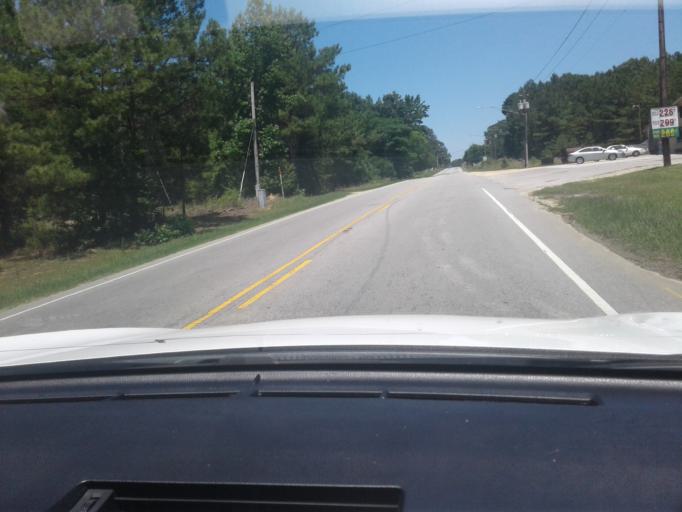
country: US
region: North Carolina
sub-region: Harnett County
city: Erwin
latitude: 35.3152
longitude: -78.6851
